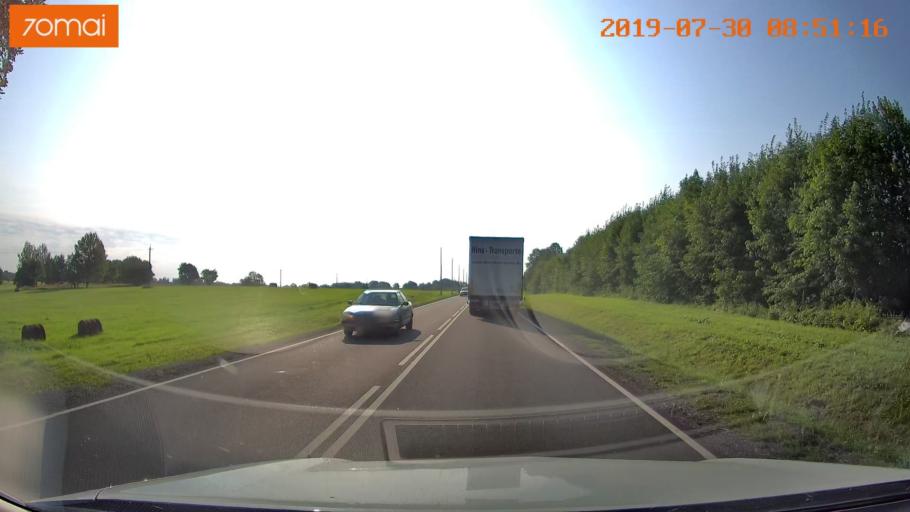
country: RU
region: Kaliningrad
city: Chernyakhovsk
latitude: 54.6033
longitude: 21.9547
